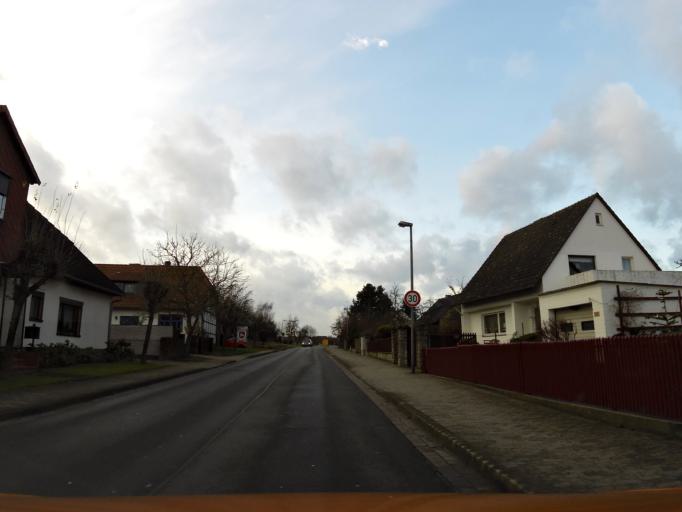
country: DE
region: Lower Saxony
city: Danndorf
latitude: 52.3927
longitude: 10.8486
